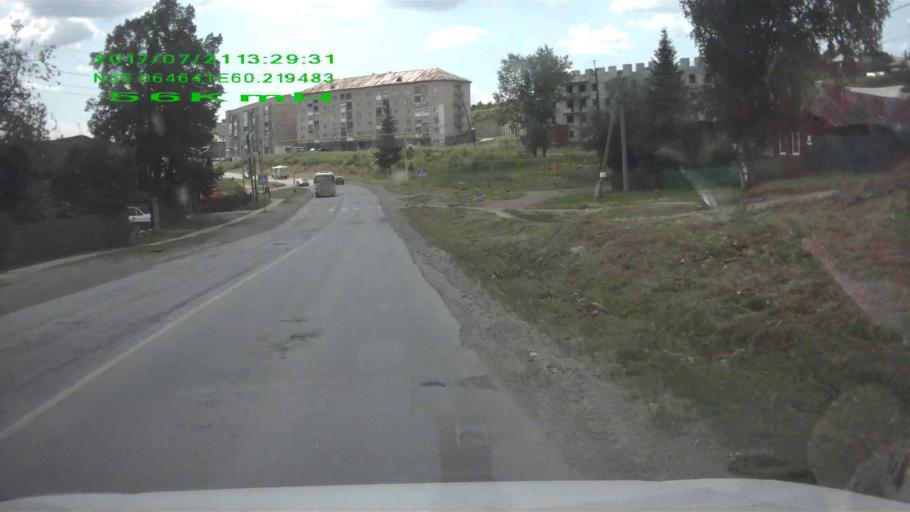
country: RU
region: Chelyabinsk
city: Verkhniy Ufaley
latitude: 56.0640
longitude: 60.2190
